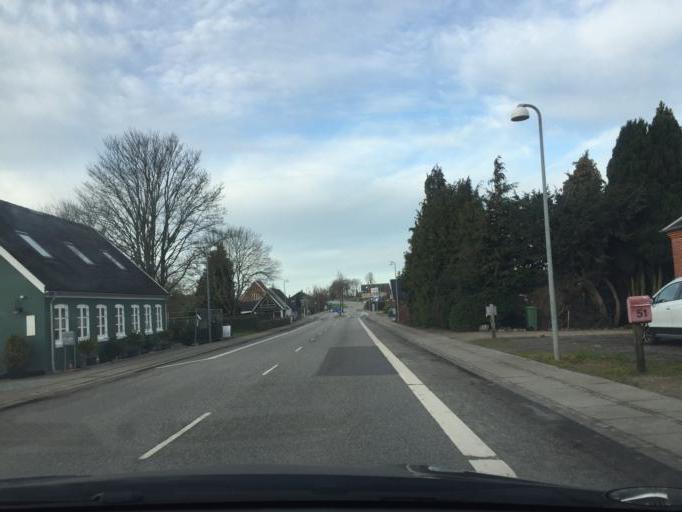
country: DK
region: South Denmark
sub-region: Faaborg-Midtfyn Kommune
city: Ringe
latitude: 55.2448
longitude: 10.4766
